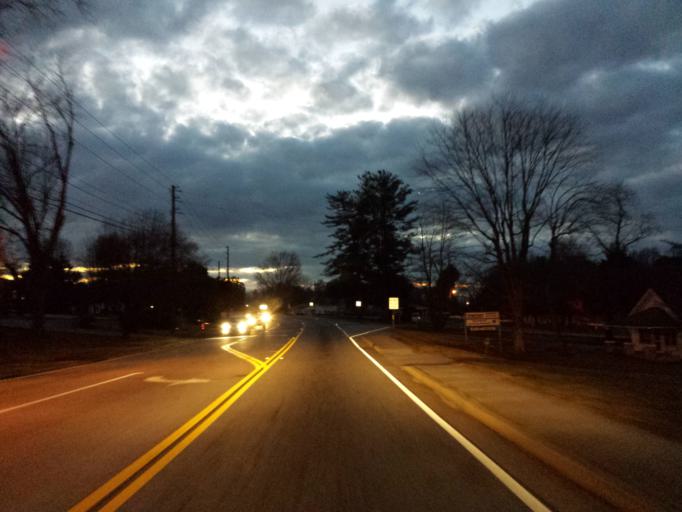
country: US
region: Georgia
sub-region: White County
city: Cleveland
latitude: 34.5968
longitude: -83.7686
